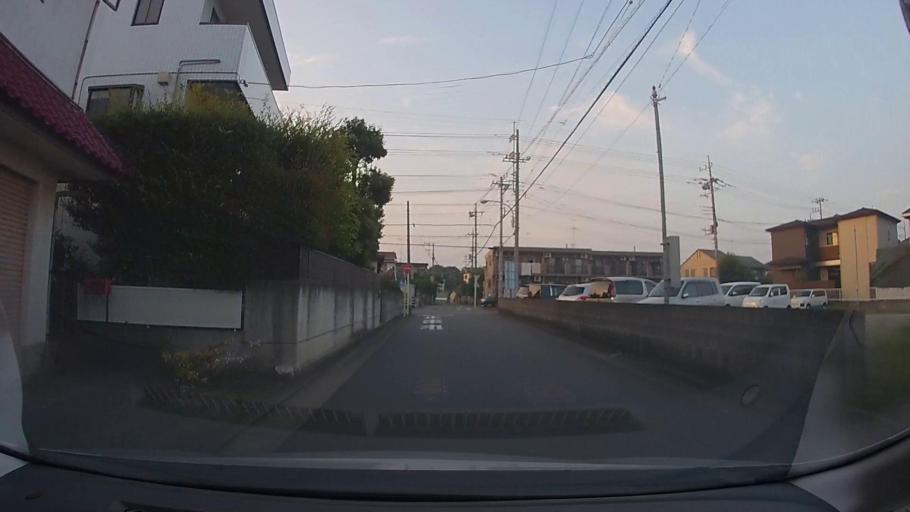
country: JP
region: Kanagawa
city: Minami-rinkan
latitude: 35.4711
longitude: 139.4681
